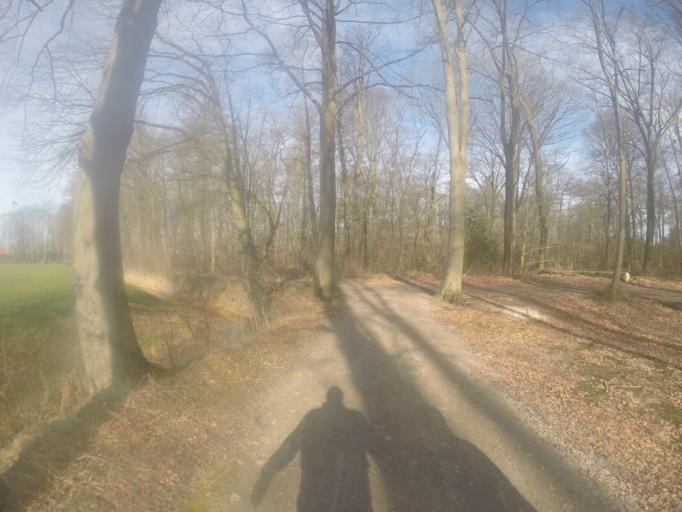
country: NL
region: Gelderland
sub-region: Gemeente Lochem
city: Lochem
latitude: 52.1190
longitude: 6.3813
